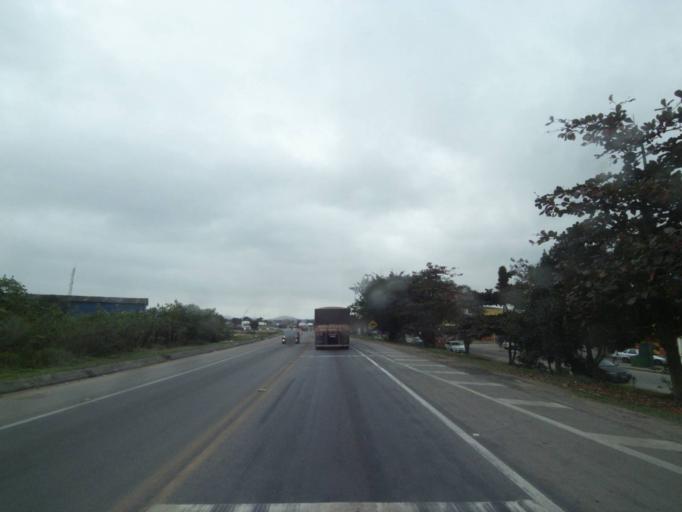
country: BR
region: Parana
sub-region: Paranagua
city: Paranagua
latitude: -25.5312
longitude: -48.5492
